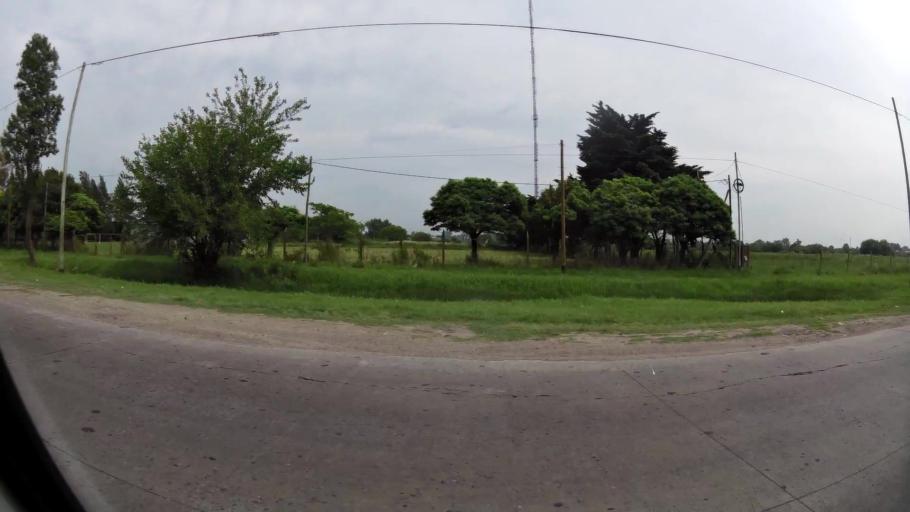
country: AR
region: Buenos Aires
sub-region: Partido de La Plata
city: La Plata
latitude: -34.9088
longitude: -58.0029
